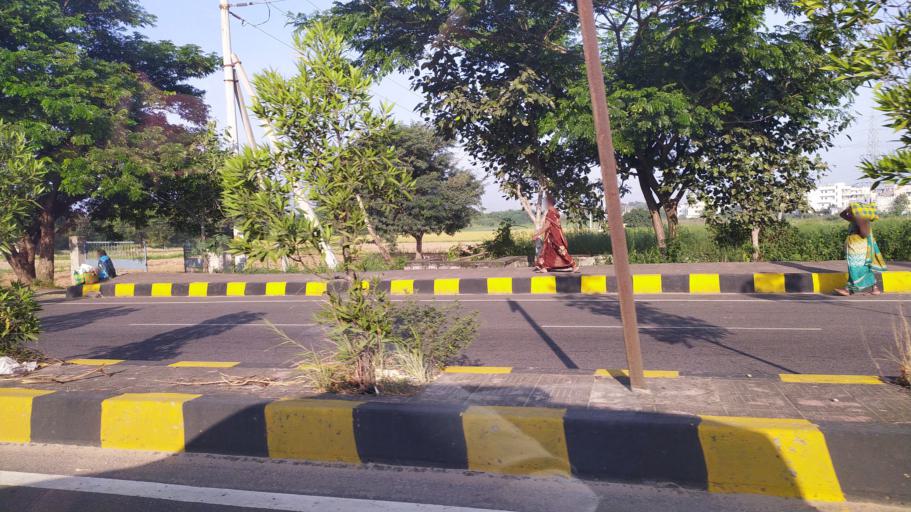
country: IN
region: Telangana
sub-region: Hyderabad
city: Hyderabad
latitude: 17.3260
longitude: 78.4080
